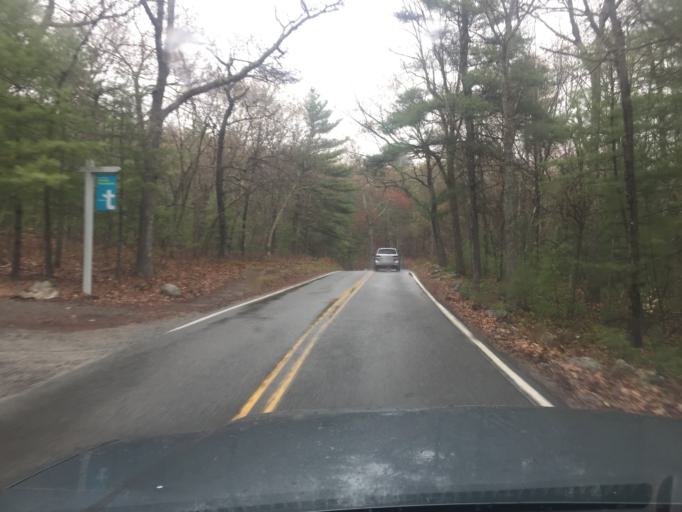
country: US
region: Massachusetts
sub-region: Norfolk County
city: Dover
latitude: 42.2281
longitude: -71.2568
